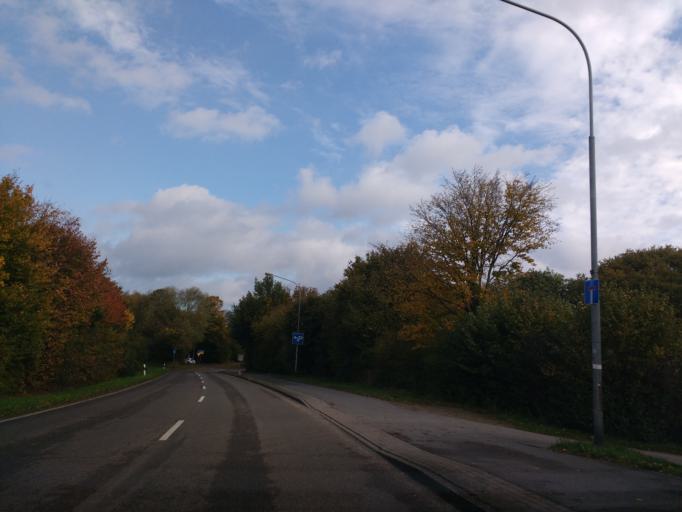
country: DE
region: Schleswig-Holstein
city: Travemuende
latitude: 53.9721
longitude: 10.8669
